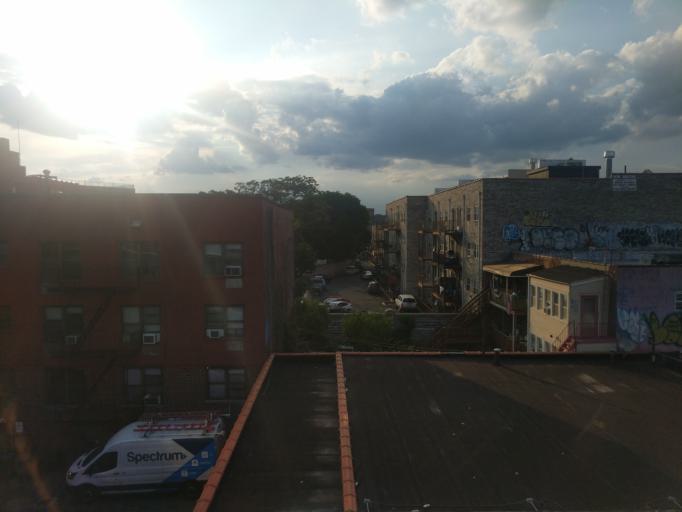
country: US
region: New York
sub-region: Bronx
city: The Bronx
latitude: 40.8349
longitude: -73.8490
